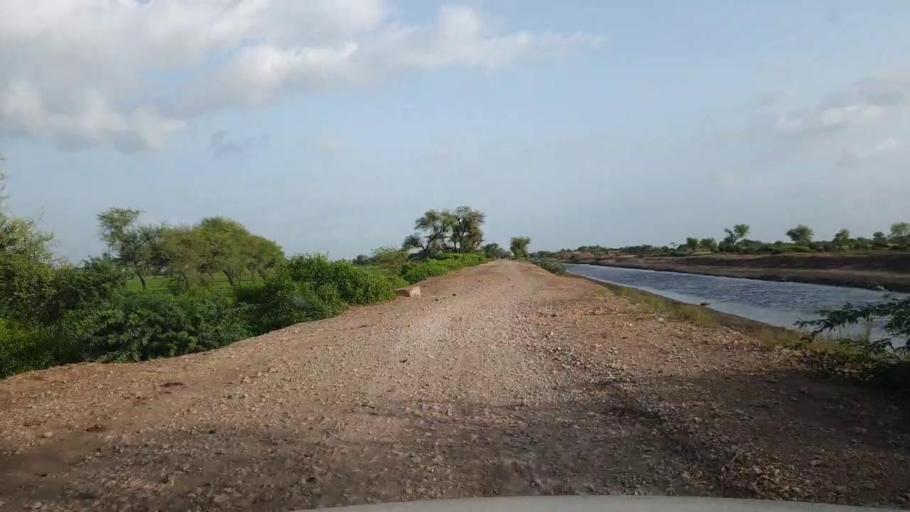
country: PK
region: Sindh
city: Kario
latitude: 24.8048
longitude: 68.6472
